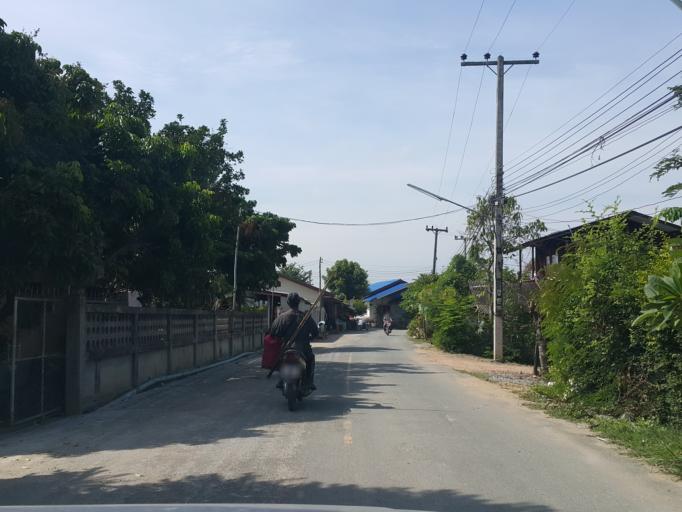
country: TH
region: Chiang Mai
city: Saraphi
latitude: 18.6982
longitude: 99.0850
